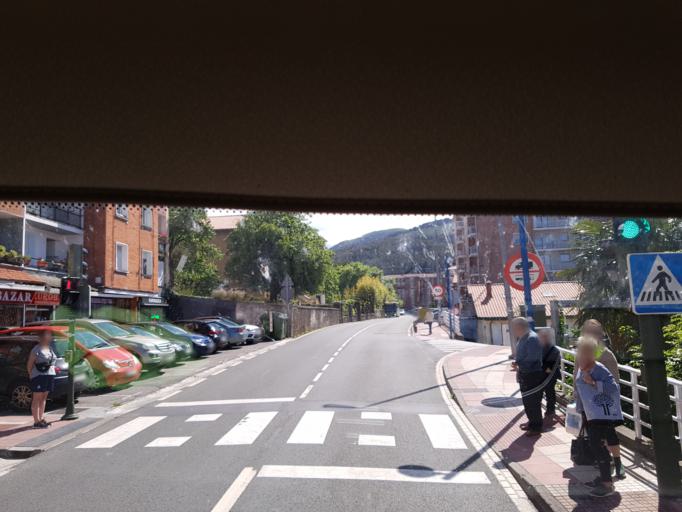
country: ES
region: Basque Country
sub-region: Bizkaia
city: San Julian de Muskiz
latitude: 43.3213
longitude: -3.1153
